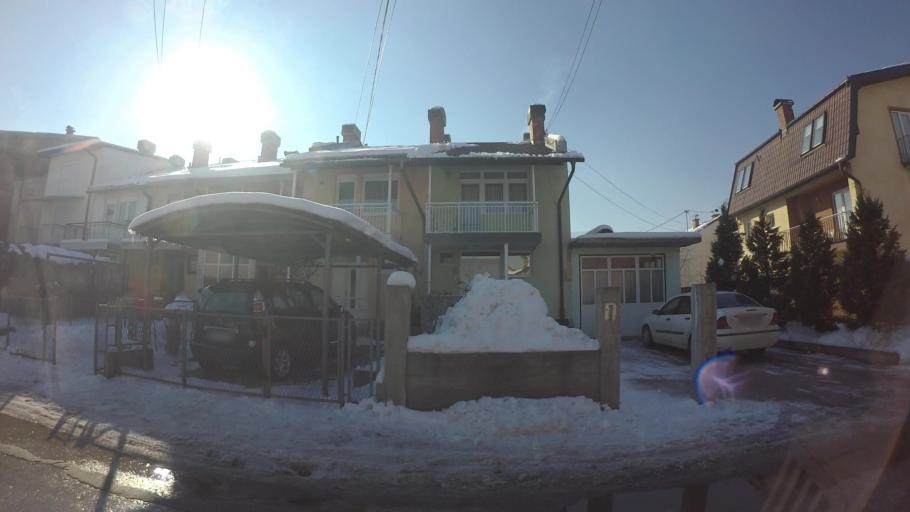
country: BA
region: Federation of Bosnia and Herzegovina
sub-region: Kanton Sarajevo
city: Sarajevo
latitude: 43.8160
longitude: 18.3160
